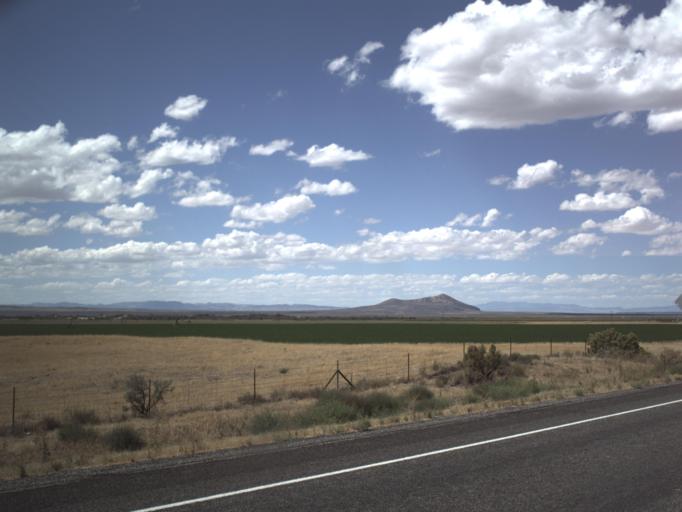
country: US
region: Utah
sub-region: Millard County
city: Fillmore
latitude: 39.1372
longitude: -112.3672
